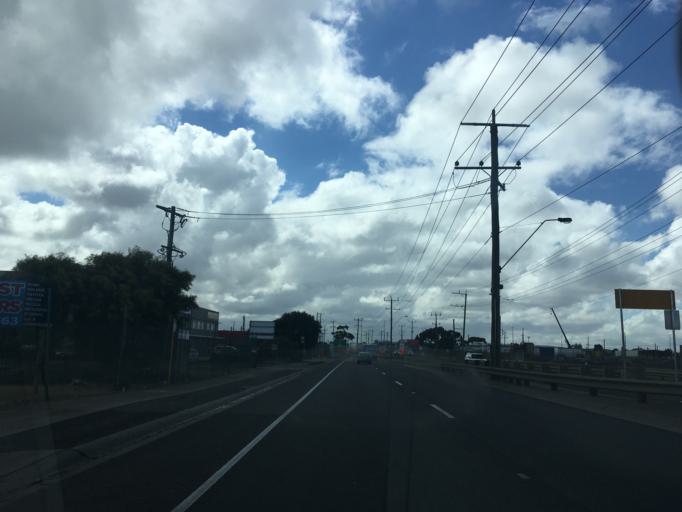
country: AU
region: Victoria
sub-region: Hobsons Bay
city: Laverton
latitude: -37.8306
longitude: 144.7849
